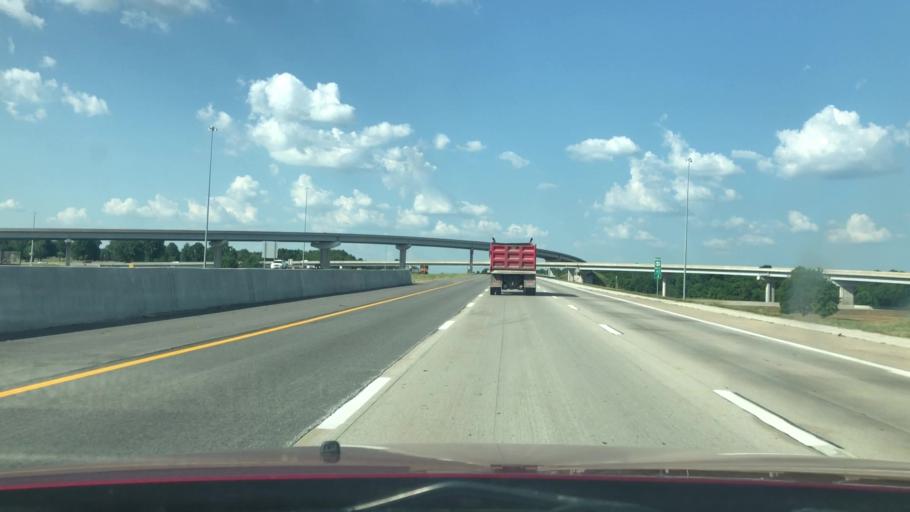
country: US
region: Missouri
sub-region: Christian County
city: Nixa
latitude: 37.1253
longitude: -93.2323
